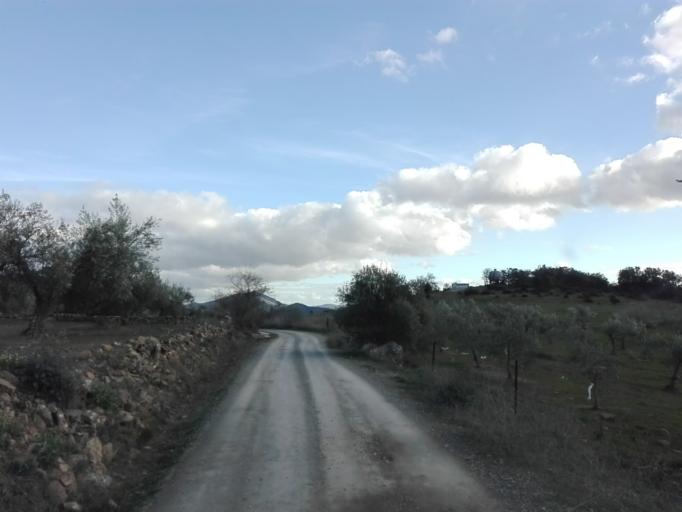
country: ES
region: Extremadura
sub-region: Provincia de Badajoz
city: Trasierra
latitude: 38.1841
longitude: -5.9848
